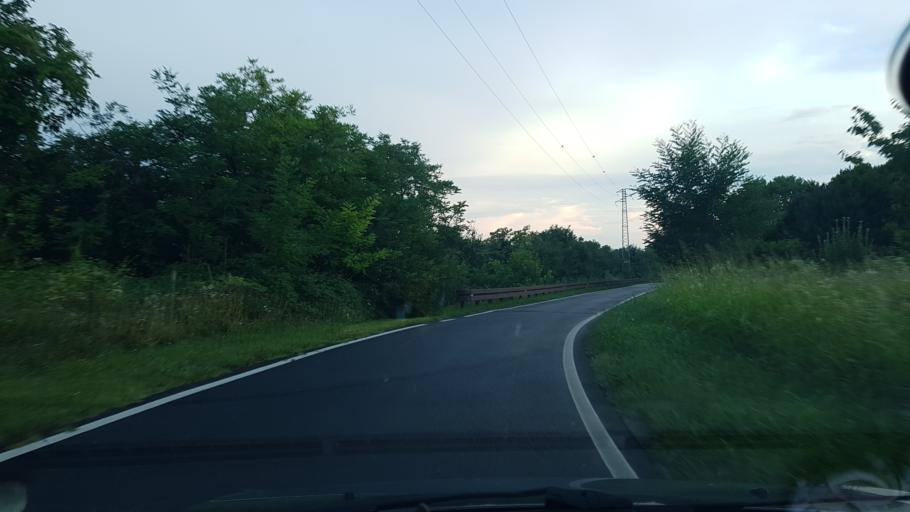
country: IT
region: Friuli Venezia Giulia
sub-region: Provincia di Gorizia
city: Savogna d'Isonzo
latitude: 45.9256
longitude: 13.5687
